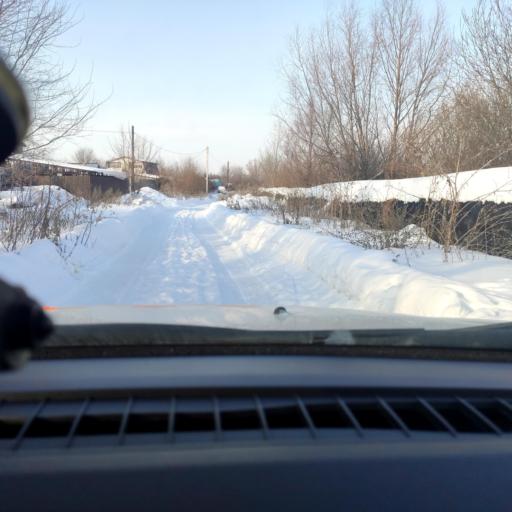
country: RU
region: Samara
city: Samara
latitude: 53.1321
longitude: 50.2589
